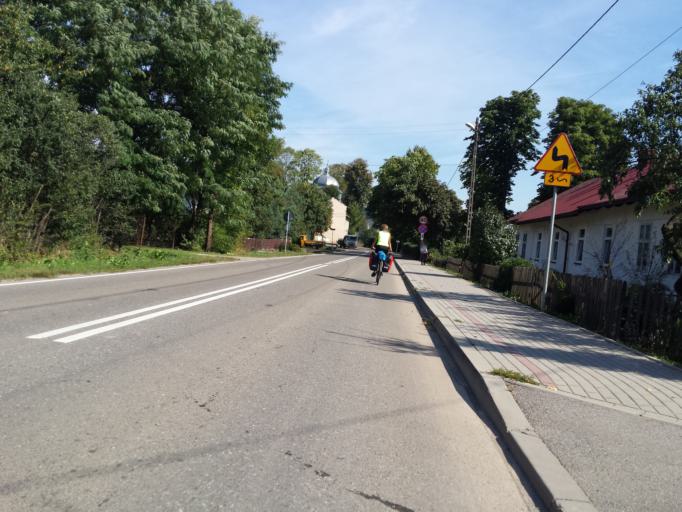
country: PL
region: Subcarpathian Voivodeship
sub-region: Powiat leski
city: Baligrod
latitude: 49.3343
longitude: 22.2870
